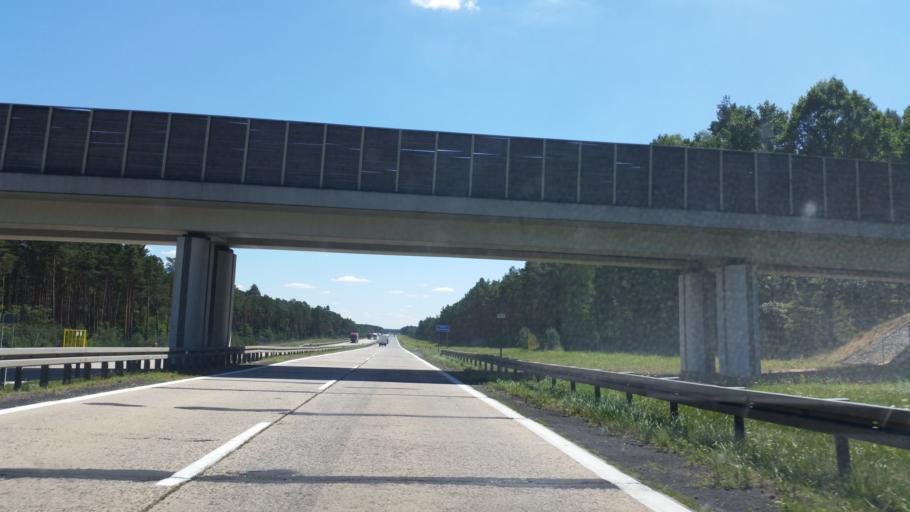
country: PL
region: Lower Silesian Voivodeship
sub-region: Powiat boleslawiecki
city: Boleslawiec
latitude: 51.3911
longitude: 15.5344
